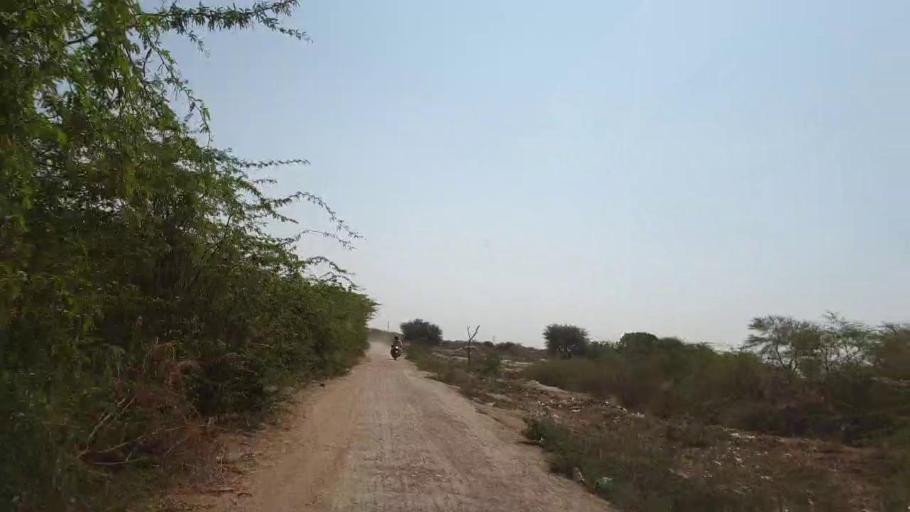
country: PK
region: Sindh
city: Kunri
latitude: 25.0856
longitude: 69.5324
